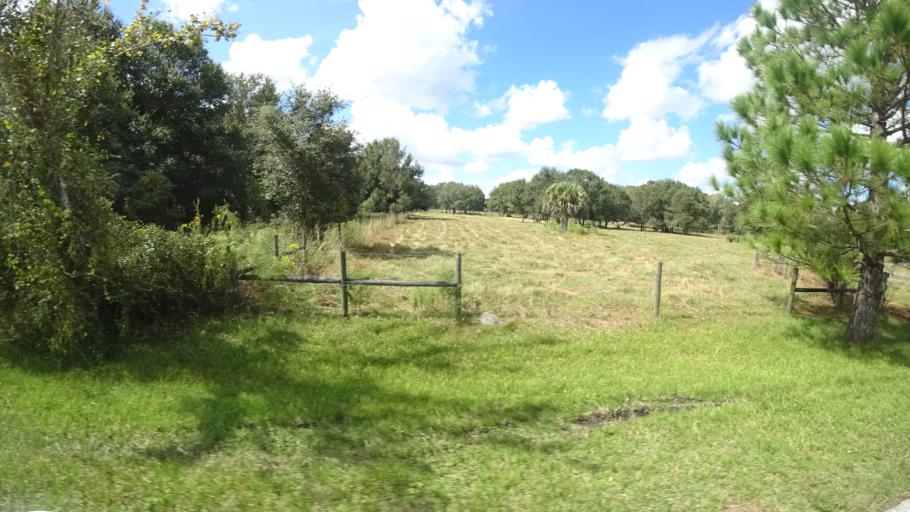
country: US
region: Florida
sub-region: Sarasota County
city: Lake Sarasota
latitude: 27.3293
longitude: -82.2695
